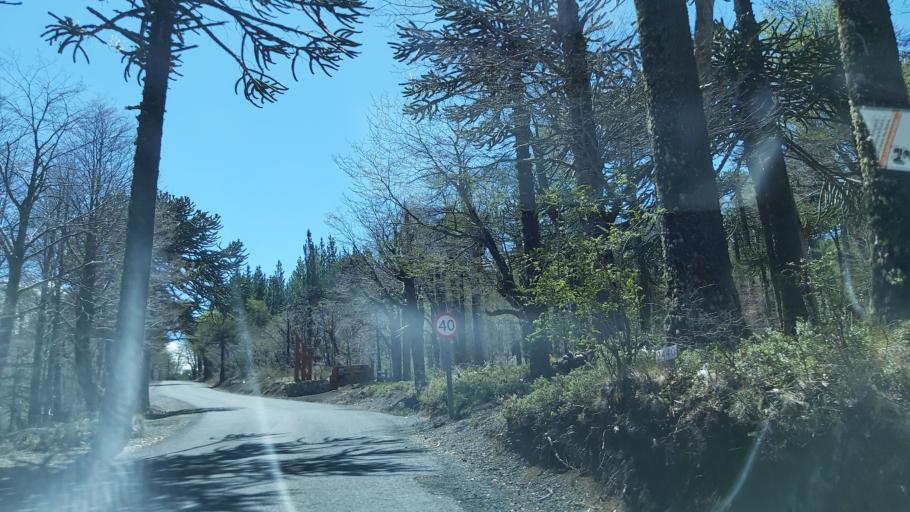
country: CL
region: Araucania
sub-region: Provincia de Cautin
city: Vilcun
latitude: -38.4318
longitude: -71.5367
